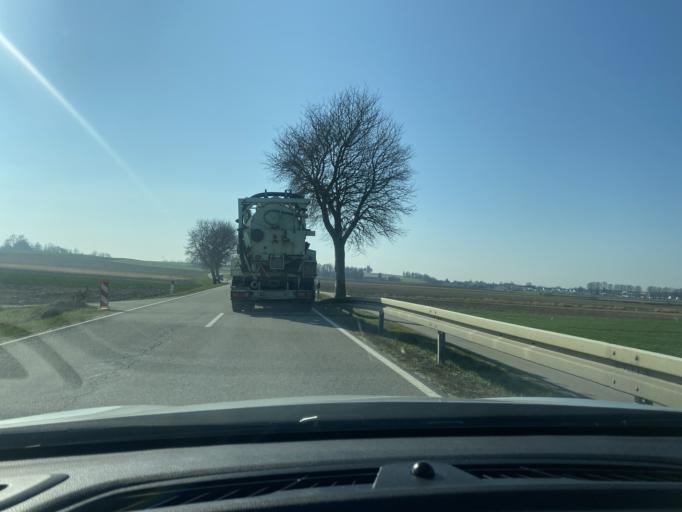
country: DE
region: Bavaria
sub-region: Upper Bavaria
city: Oberding
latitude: 48.2974
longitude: 11.8477
